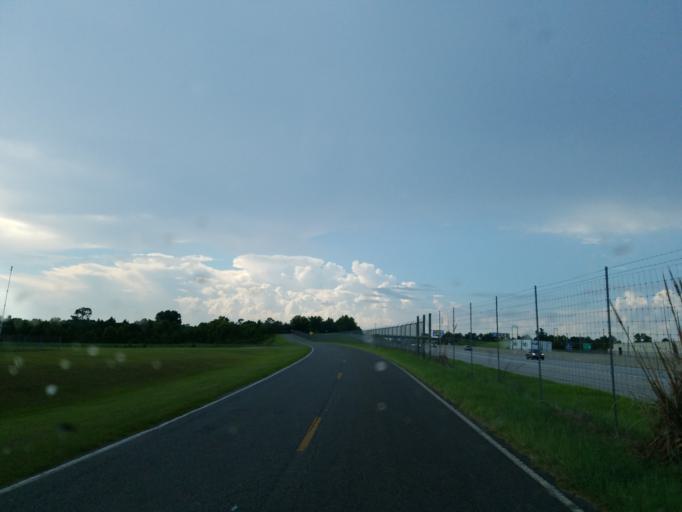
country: US
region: Georgia
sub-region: Cook County
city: Adel
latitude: 31.1093
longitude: -83.4265
